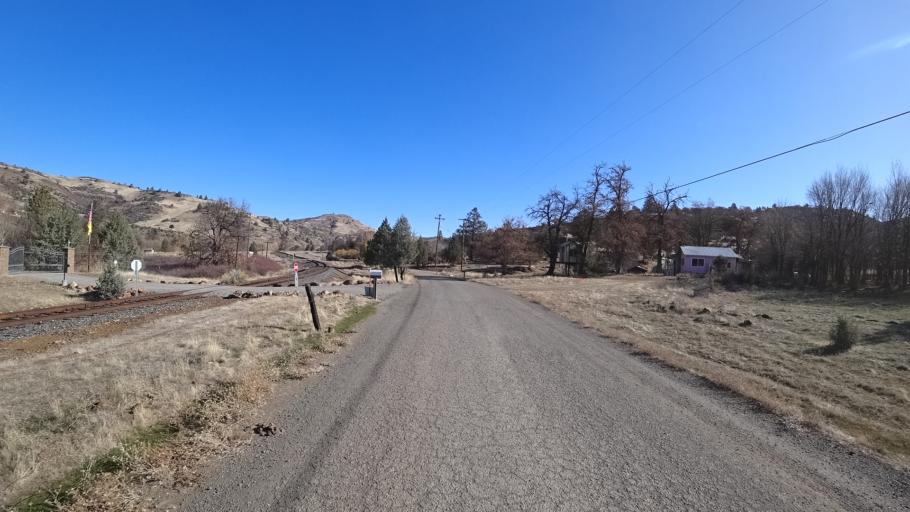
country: US
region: California
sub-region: Siskiyou County
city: Montague
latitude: 41.8946
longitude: -122.5201
